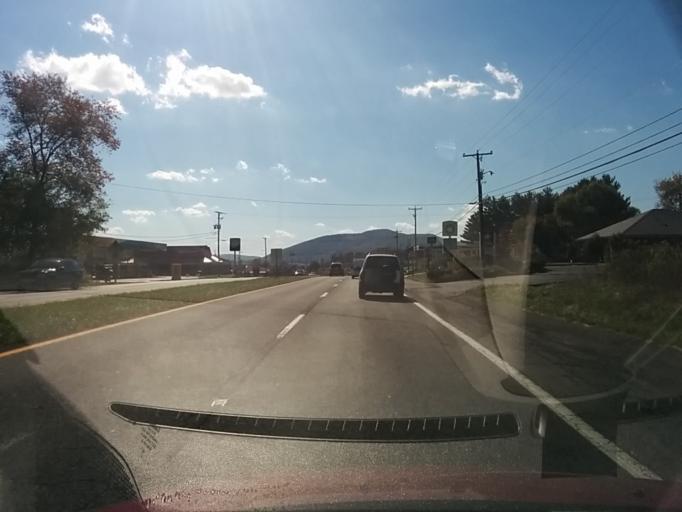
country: US
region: Virginia
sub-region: Botetourt County
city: Daleville
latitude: 37.3941
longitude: -79.9066
